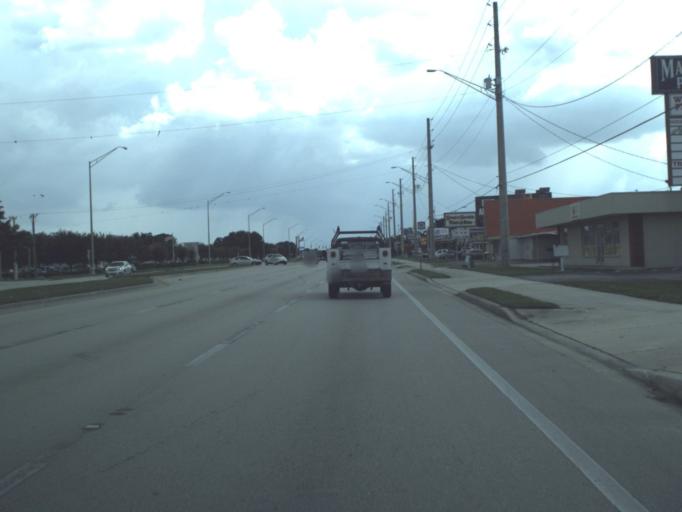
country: US
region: Florida
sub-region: Polk County
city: Gibsonia
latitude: 28.1051
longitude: -81.9739
